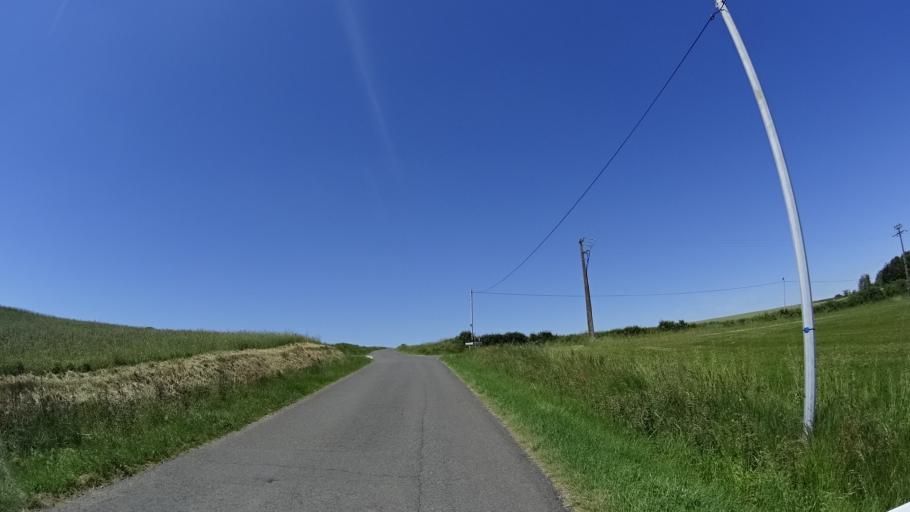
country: FR
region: Pays de la Loire
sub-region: Departement de Maine-et-Loire
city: Chenehutte-Treves-Cunault
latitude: 47.2841
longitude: -0.1388
